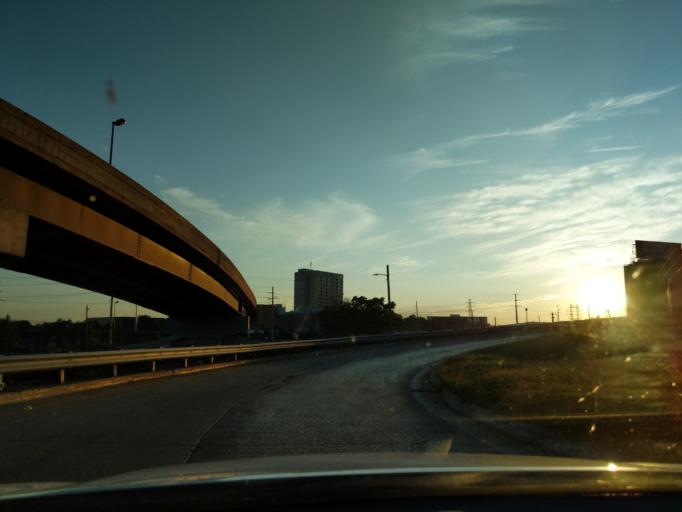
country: US
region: Missouri
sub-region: City of Saint Louis
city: St. Louis
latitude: 38.6208
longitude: -90.1920
